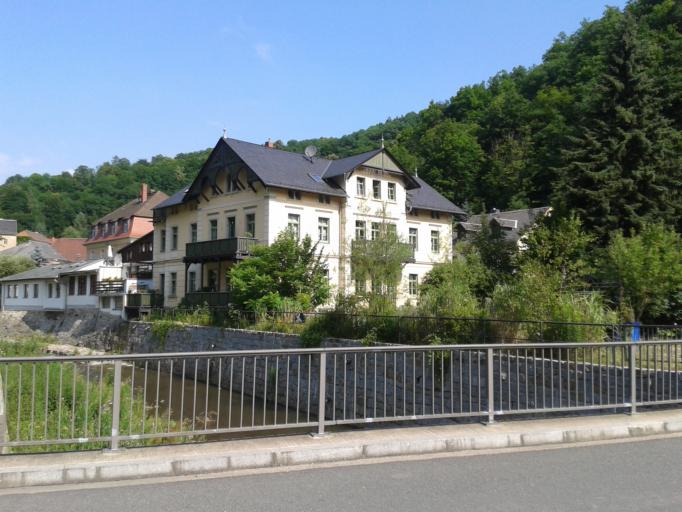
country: DE
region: Saxony
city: Tharandt
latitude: 50.9825
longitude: 13.5861
